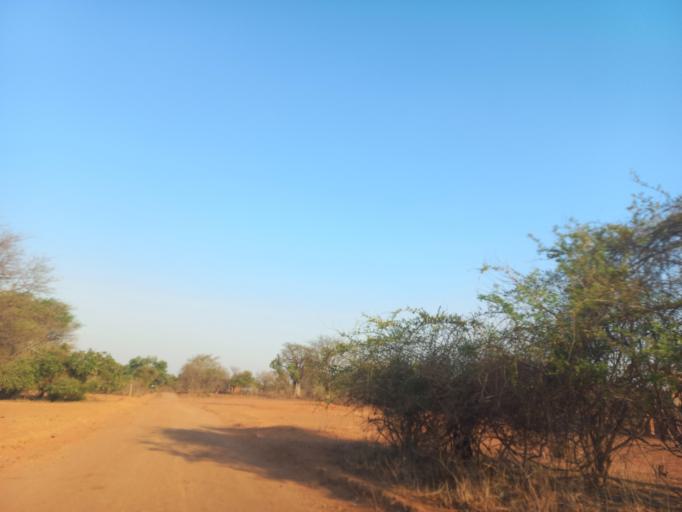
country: ZM
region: Lusaka
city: Luangwa
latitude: -15.4342
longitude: 30.3469
